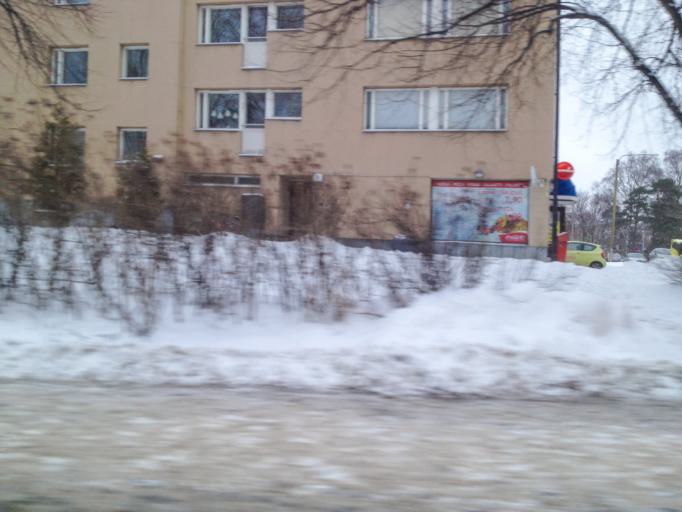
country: FI
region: Uusimaa
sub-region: Helsinki
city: Vantaa
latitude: 60.1956
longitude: 25.0535
